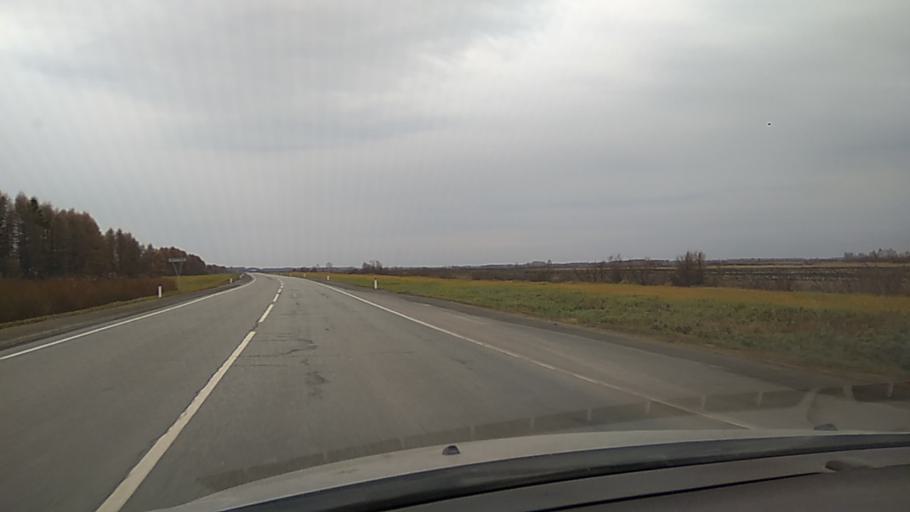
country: RU
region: Sverdlovsk
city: Pyshma
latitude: 57.0422
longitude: 63.4338
